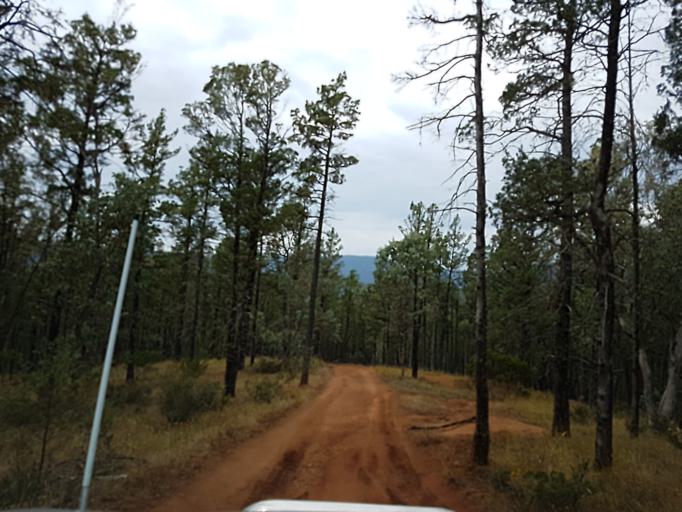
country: AU
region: New South Wales
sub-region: Snowy River
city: Jindabyne
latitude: -36.9297
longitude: 148.3946
